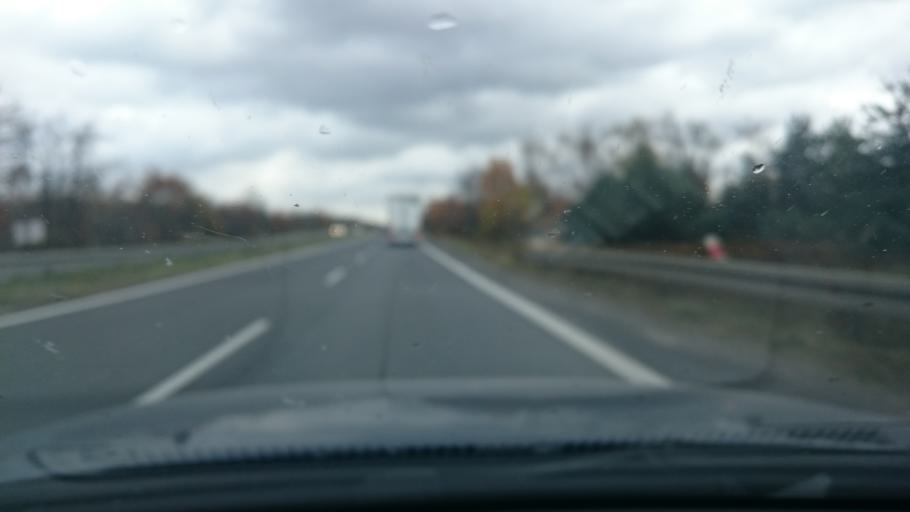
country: PL
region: Lesser Poland Voivodeship
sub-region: Powiat olkuski
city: Boleslaw
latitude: 50.2929
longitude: 19.5035
